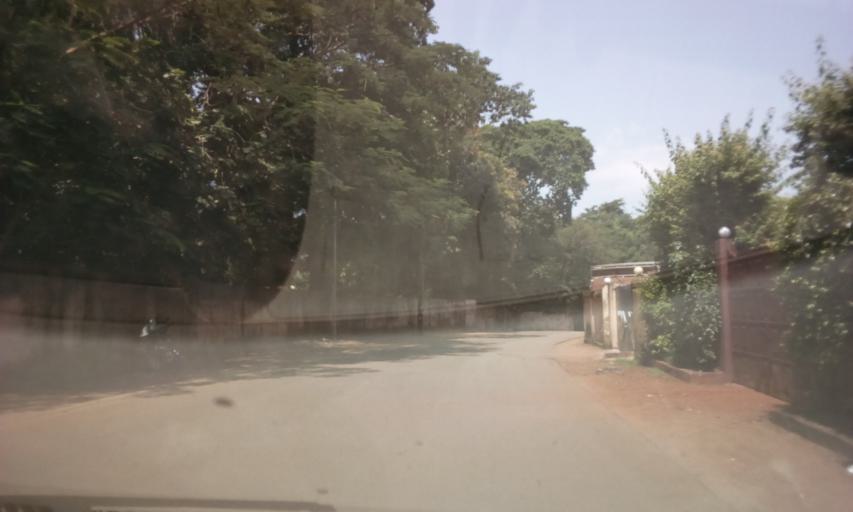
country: GN
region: Conakry
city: Conakry
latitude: 9.5689
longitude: -13.6652
